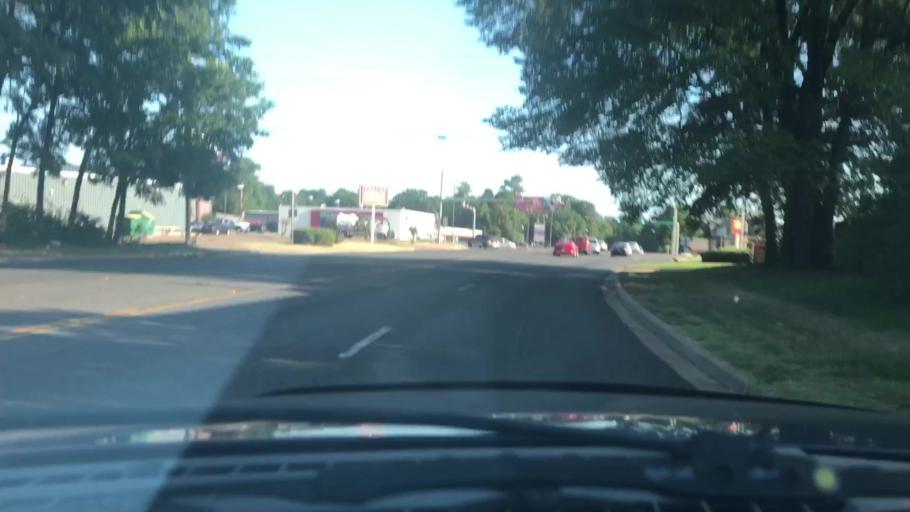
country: US
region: Texas
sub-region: Bowie County
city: Texarkana
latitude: 33.4339
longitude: -94.0628
